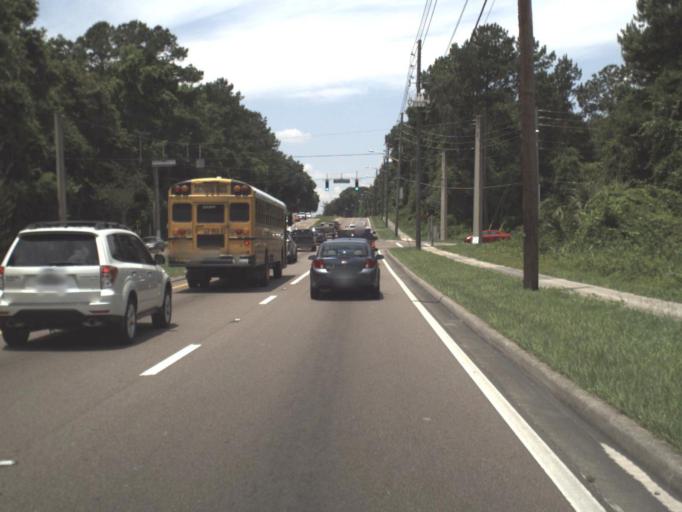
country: US
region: Florida
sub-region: Alachua County
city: Alachua
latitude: 29.6604
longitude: -82.4326
